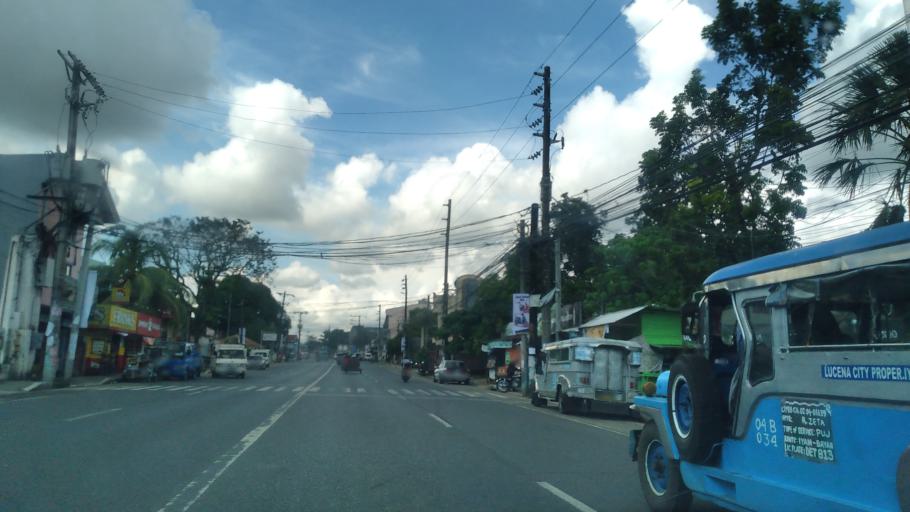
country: PH
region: Calabarzon
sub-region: Province of Quezon
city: Isabang
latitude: 13.9481
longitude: 121.5853
